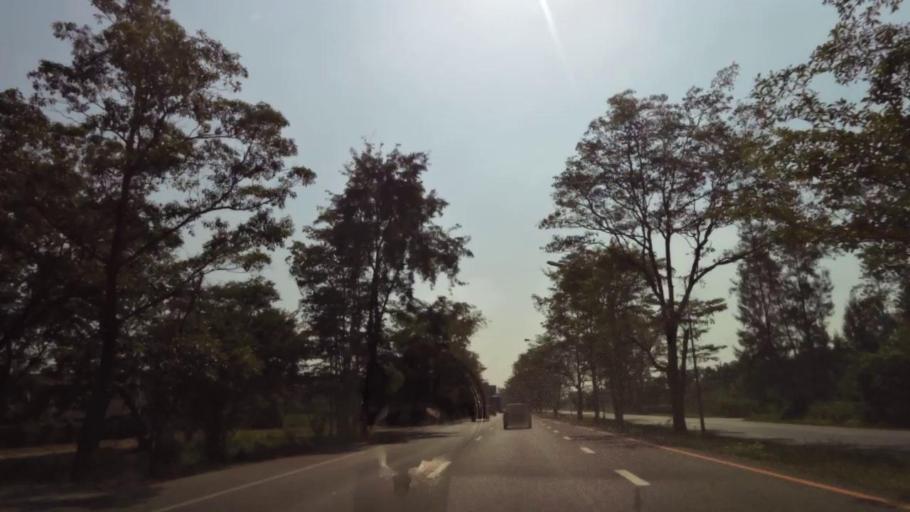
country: TH
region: Phichit
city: Bueng Na Rang
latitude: 16.0341
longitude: 100.1162
